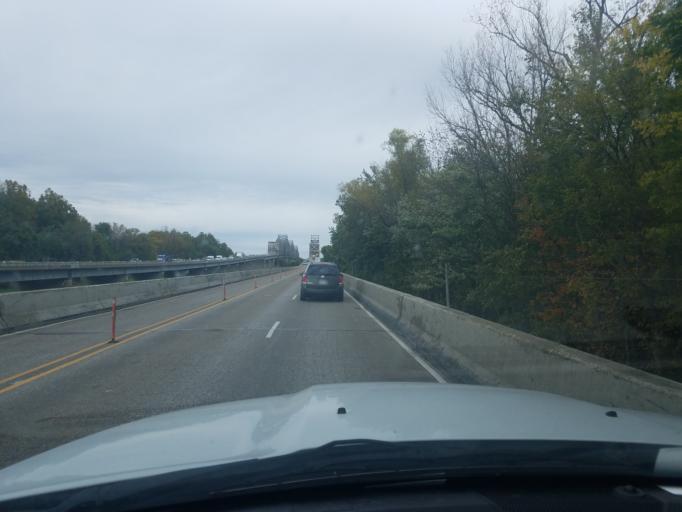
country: US
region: Kentucky
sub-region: Henderson County
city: Henderson
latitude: 37.8977
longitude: -87.5534
